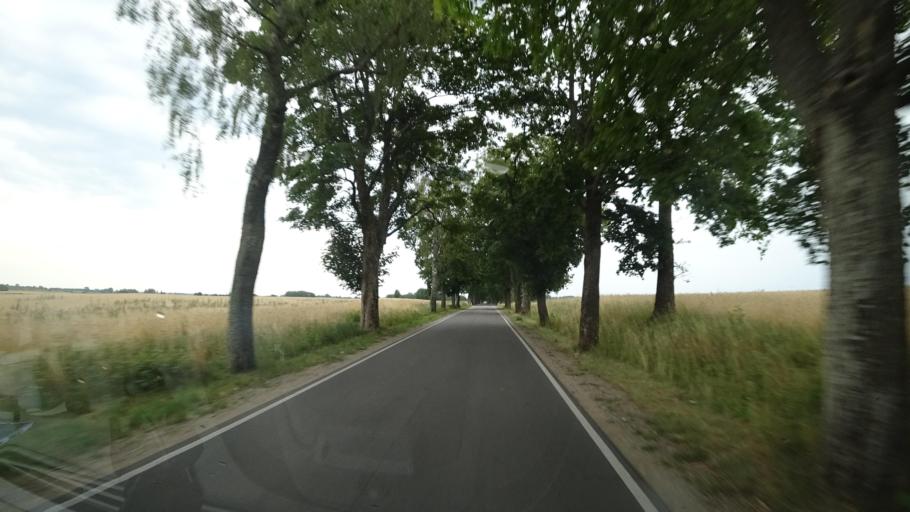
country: PL
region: Warmian-Masurian Voivodeship
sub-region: Powiat mragowski
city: Mikolajki
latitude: 53.8604
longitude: 21.6056
